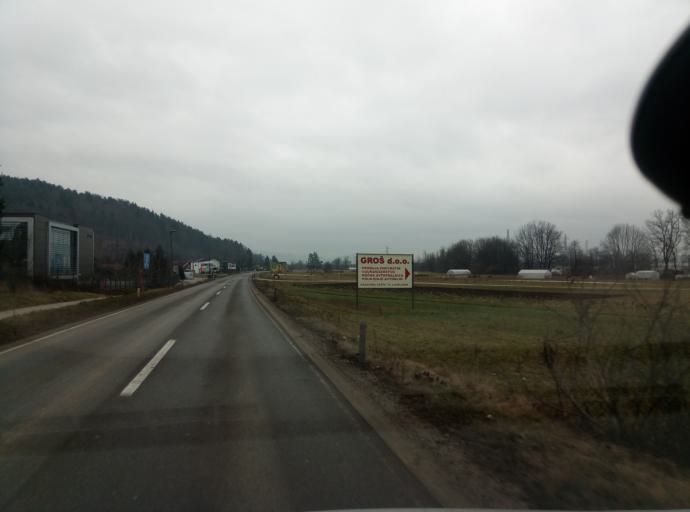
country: SI
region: Trzin
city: Trzin
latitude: 46.0994
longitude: 14.5551
